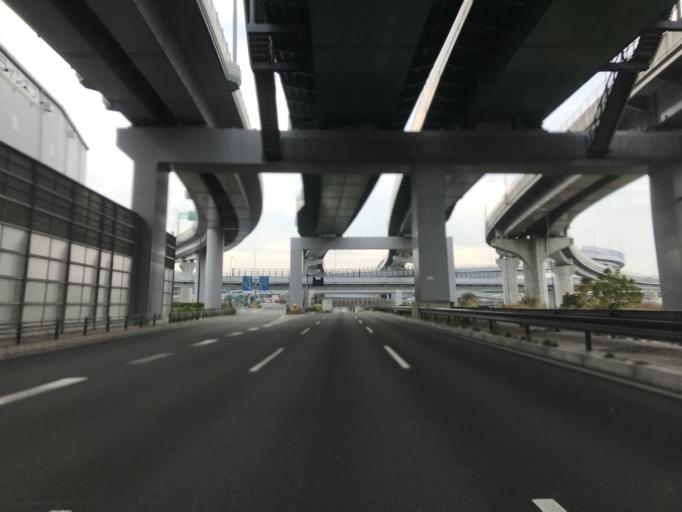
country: JP
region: Aichi
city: Iwakura
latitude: 35.2242
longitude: 136.8540
